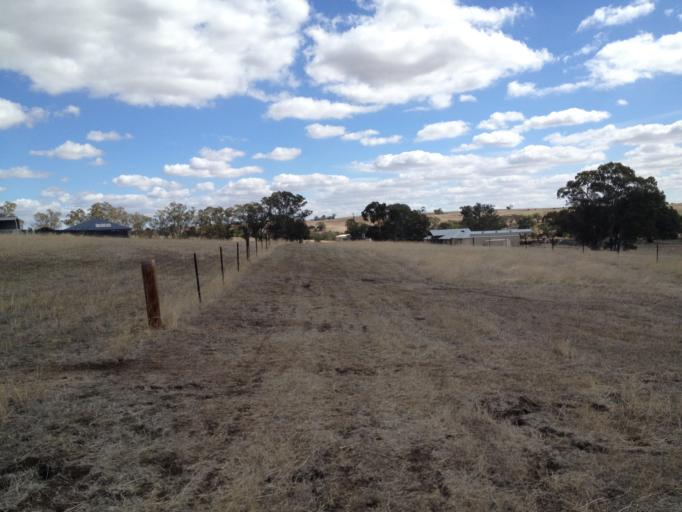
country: AU
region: South Australia
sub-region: Barossa
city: Lyndoch
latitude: -34.6291
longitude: 138.8361
